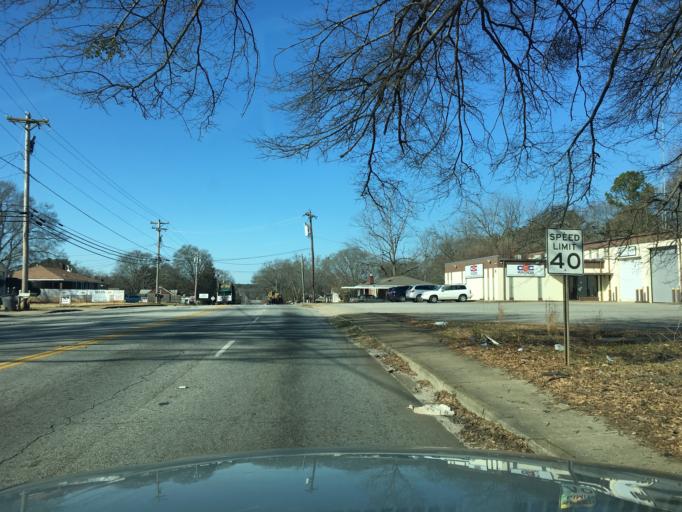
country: US
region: South Carolina
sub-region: Greenville County
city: Sans Souci
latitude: 34.8942
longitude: -82.4328
